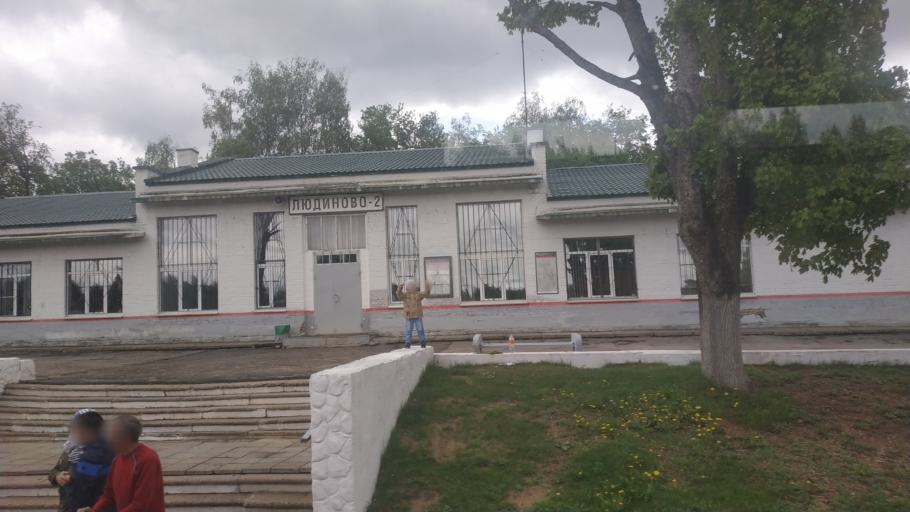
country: RU
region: Kaluga
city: Lyudinovo
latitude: 53.8879
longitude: 34.4266
